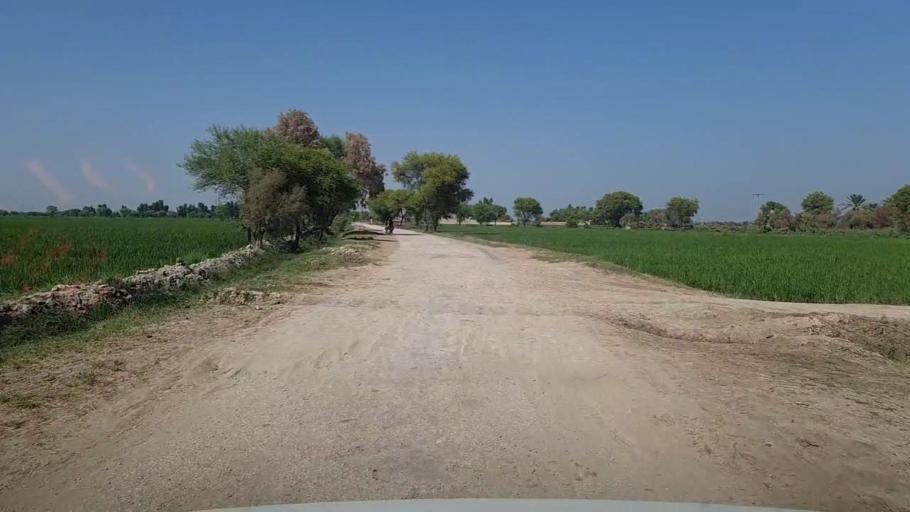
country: PK
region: Sindh
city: Kandhkot
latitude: 28.3262
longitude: 69.3669
